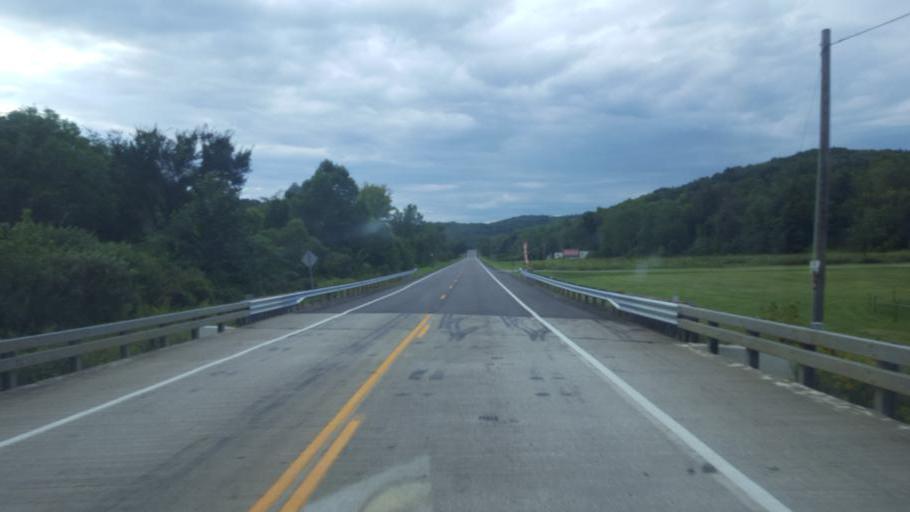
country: US
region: Ohio
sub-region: Knox County
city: Oak Hill
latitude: 40.4609
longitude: -82.1759
